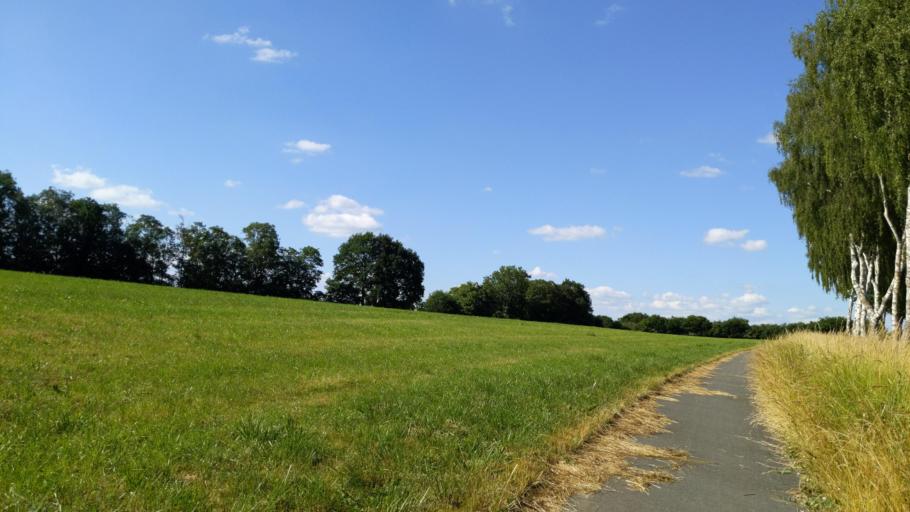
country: DE
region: Schleswig-Holstein
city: Goldenitz
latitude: 53.7172
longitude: 10.6451
